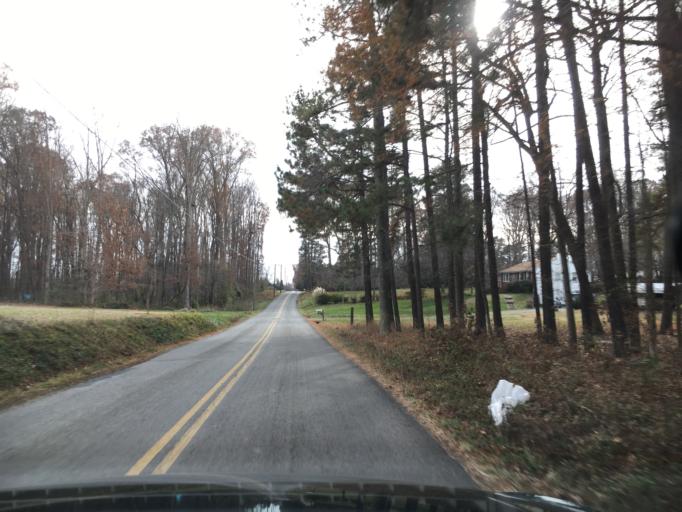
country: US
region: Virginia
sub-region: Henrico County
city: Wyndham
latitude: 37.6953
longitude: -77.6834
